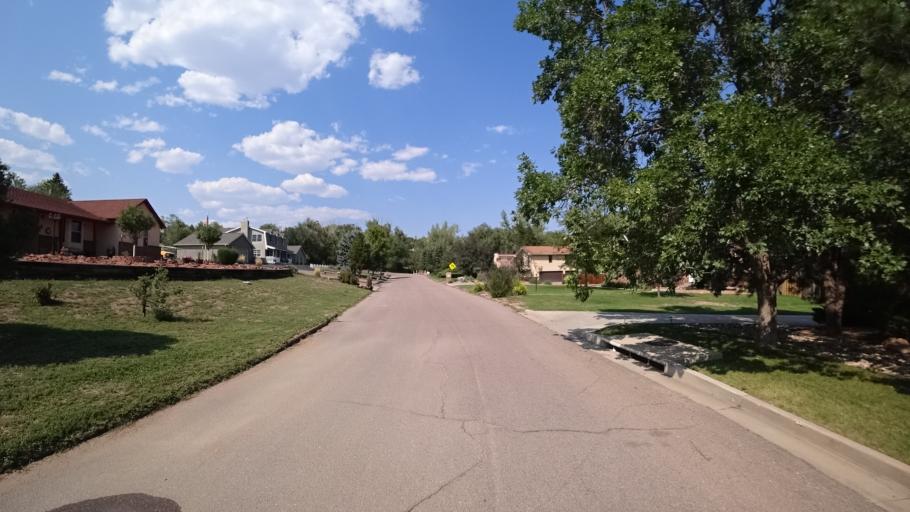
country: US
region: Colorado
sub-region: El Paso County
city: Colorado Springs
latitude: 38.7990
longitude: -104.8246
